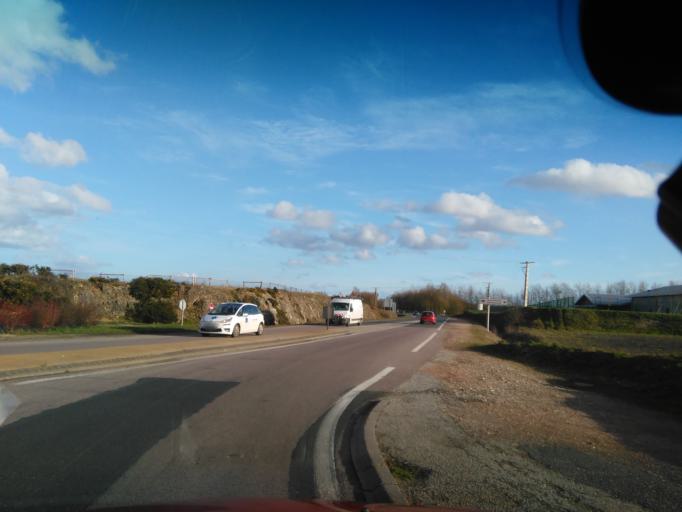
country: FR
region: Lower Normandy
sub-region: Departement du Calvados
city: Falaise
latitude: 48.8864
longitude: -0.2188
